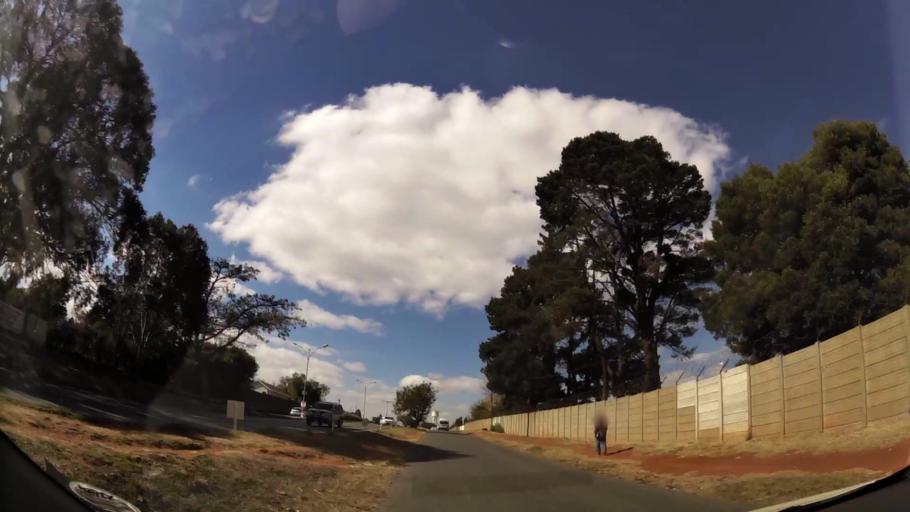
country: ZA
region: Gauteng
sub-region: West Rand District Municipality
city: Krugersdorp
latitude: -26.1125
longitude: 27.8067
